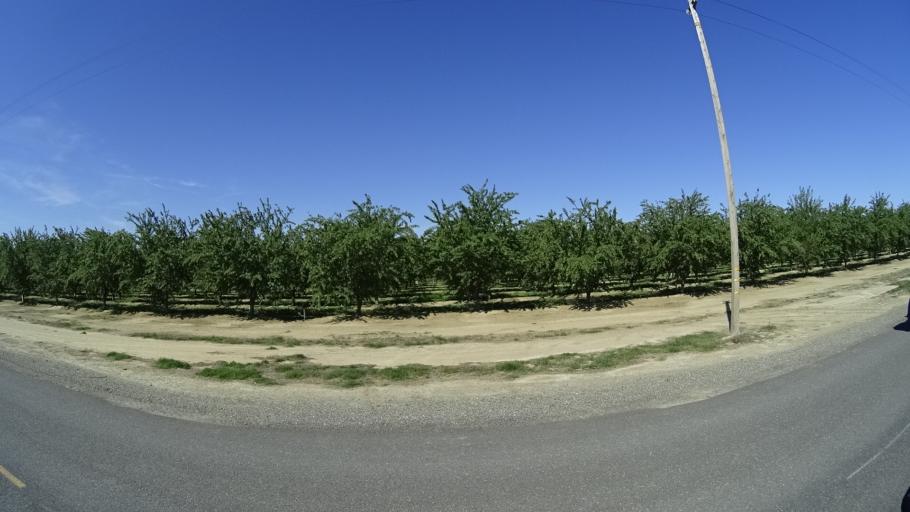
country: US
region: California
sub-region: Glenn County
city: Hamilton City
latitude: 39.6805
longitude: -122.1033
